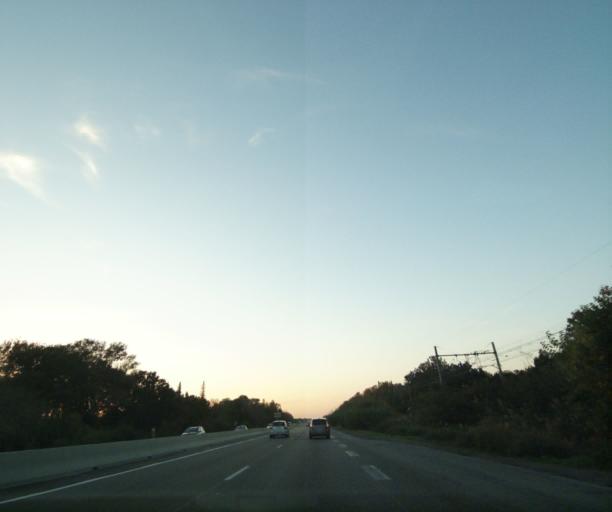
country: FR
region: Provence-Alpes-Cote d'Azur
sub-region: Departement des Bouches-du-Rhone
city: Fontvieille
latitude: 43.6402
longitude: 4.7211
